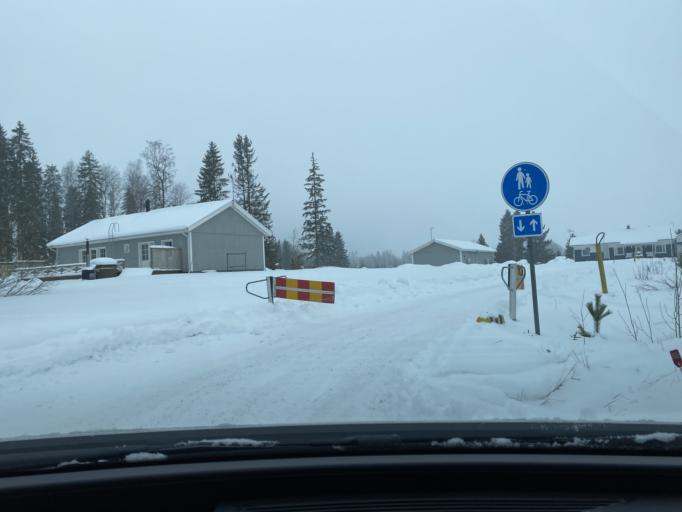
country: FI
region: Pirkanmaa
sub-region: Lounais-Pirkanmaa
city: Punkalaidun
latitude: 61.1226
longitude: 23.0892
